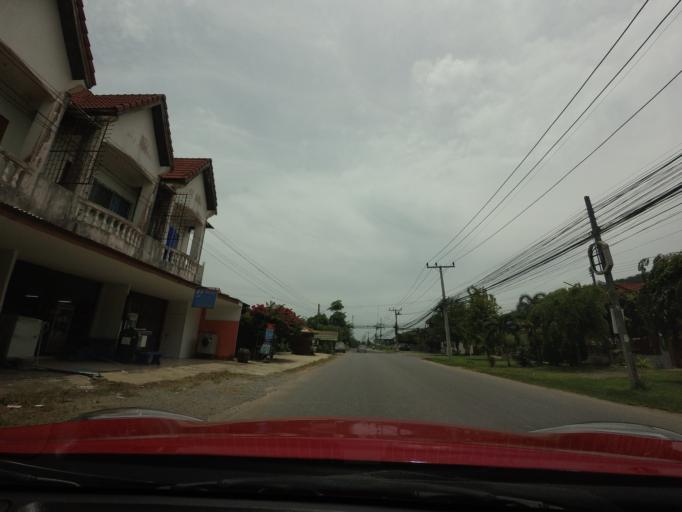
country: TH
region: Songkhla
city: Hat Yai
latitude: 7.0014
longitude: 100.5256
